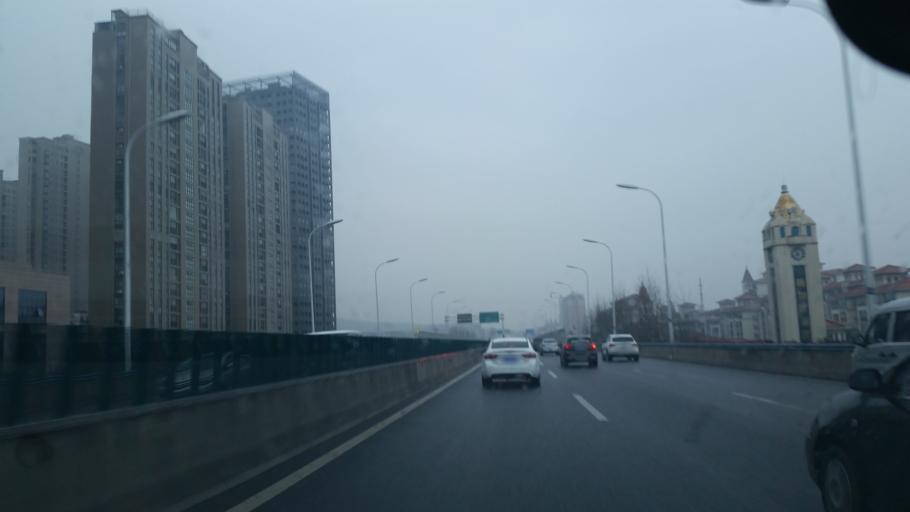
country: CN
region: Anhui Sheng
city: Hefei
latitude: 31.8561
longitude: 117.1924
